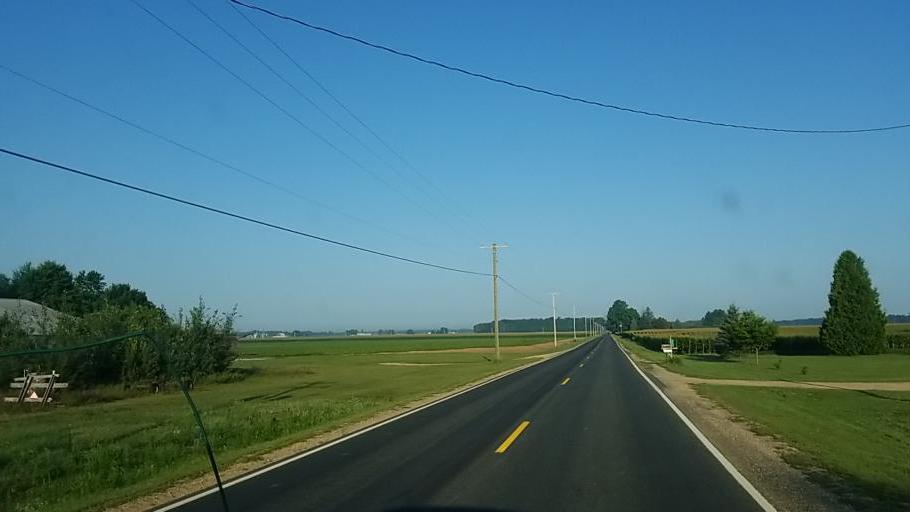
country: US
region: Michigan
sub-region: Montcalm County
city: Howard City
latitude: 43.3666
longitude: -85.4120
